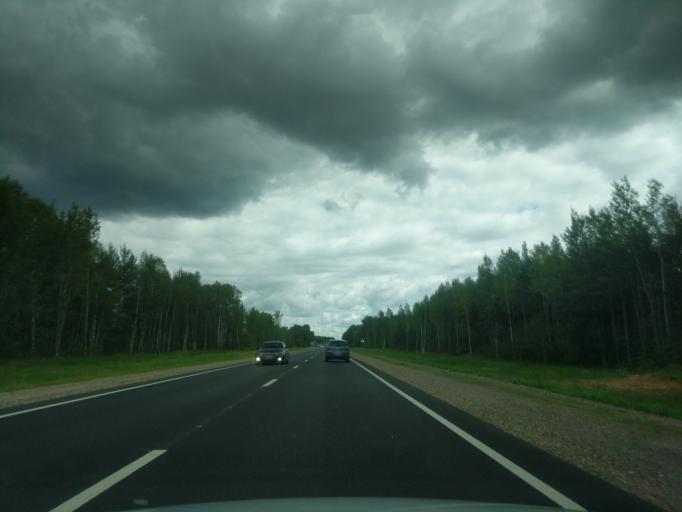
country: RU
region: Jaroslavl
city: Tunoshna
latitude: 57.5432
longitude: 40.1445
